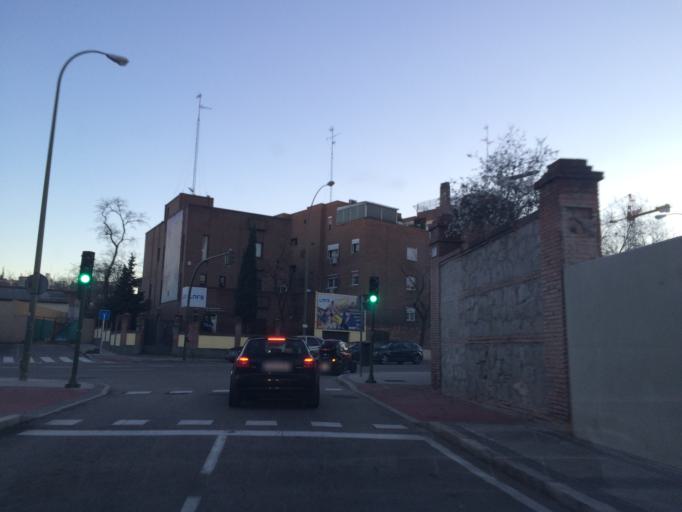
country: ES
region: Madrid
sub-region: Provincia de Madrid
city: Chamartin
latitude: 40.4676
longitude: -3.6829
